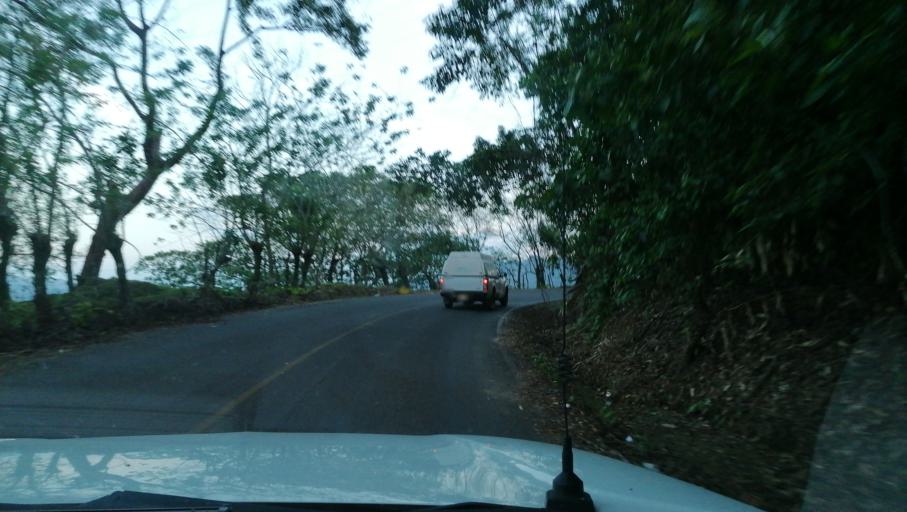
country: MX
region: Chiapas
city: Ostuacan
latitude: 17.4240
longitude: -93.3410
